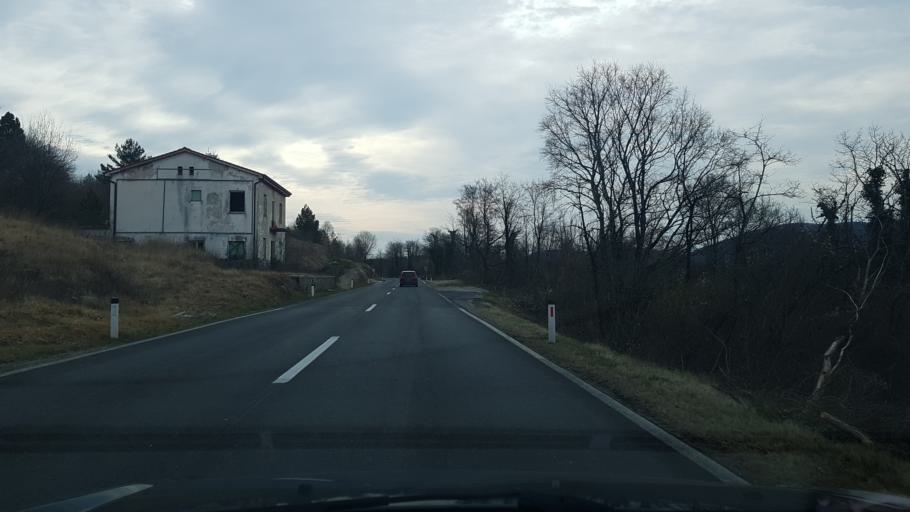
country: SI
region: Ilirska Bistrica
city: Ilirska Bistrica
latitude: 45.4998
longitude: 14.1843
